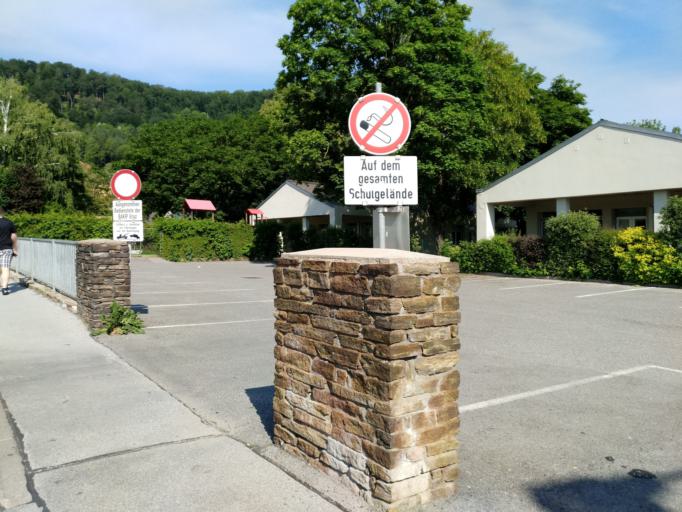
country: AT
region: Styria
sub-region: Graz Stadt
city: Wetzelsdorf
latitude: 47.0466
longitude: 15.3889
